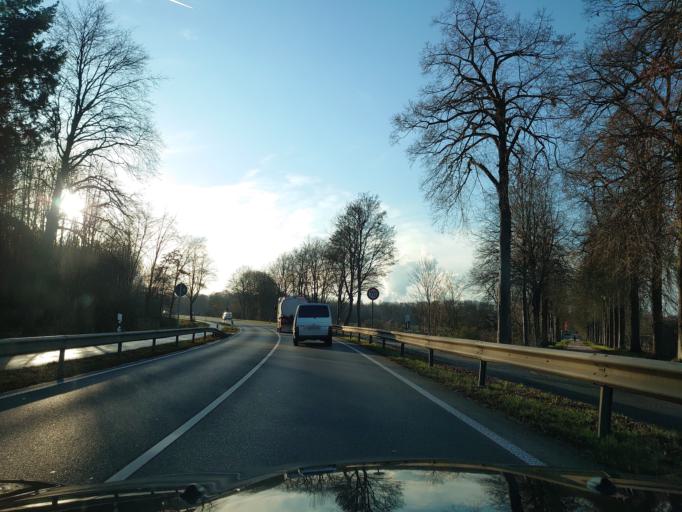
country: DE
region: North Rhine-Westphalia
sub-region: Regierungsbezirk Dusseldorf
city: Dormagen
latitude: 51.0769
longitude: 6.7618
